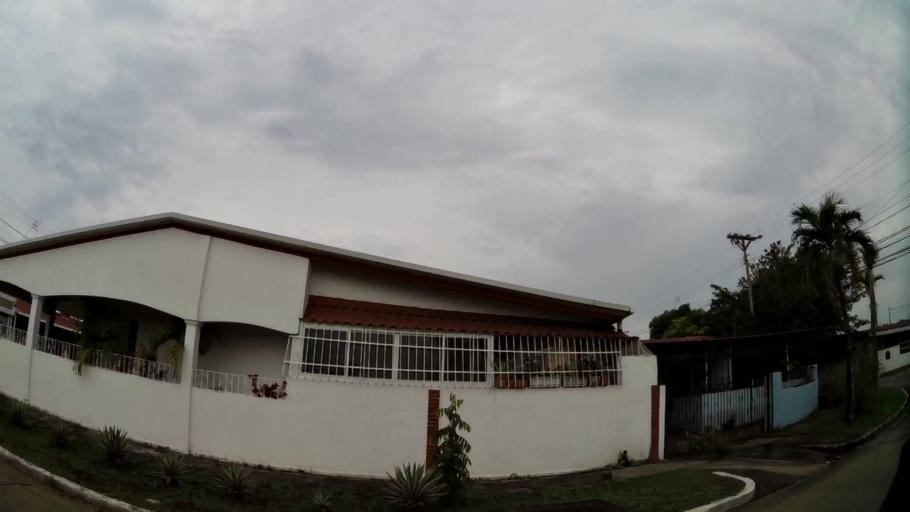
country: PA
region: Panama
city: San Miguelito
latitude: 9.0342
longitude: -79.4748
